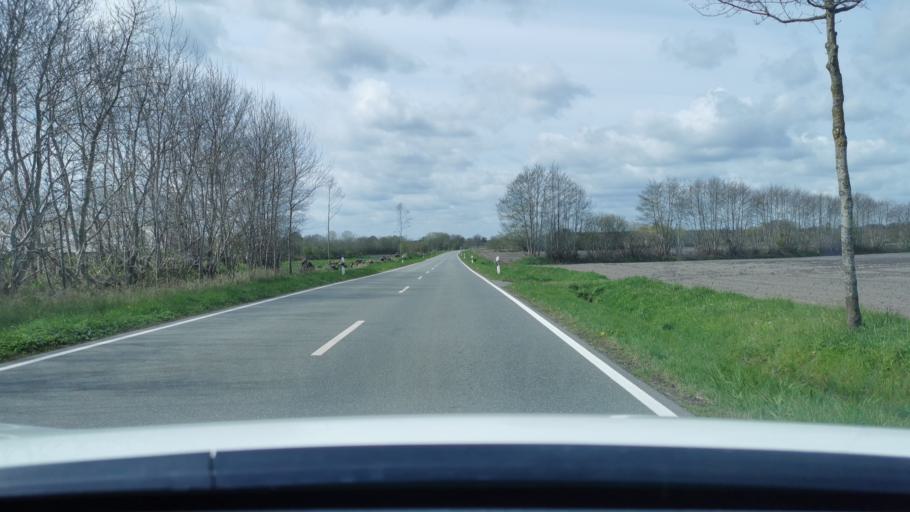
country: DE
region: Schleswig-Holstein
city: Breiholz
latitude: 54.1983
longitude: 9.5097
